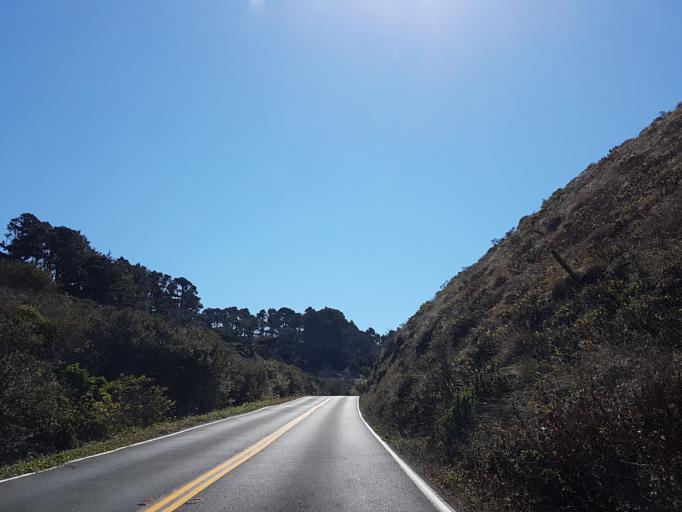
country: US
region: California
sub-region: Sonoma County
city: Sea Ranch
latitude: 38.9054
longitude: -123.6923
